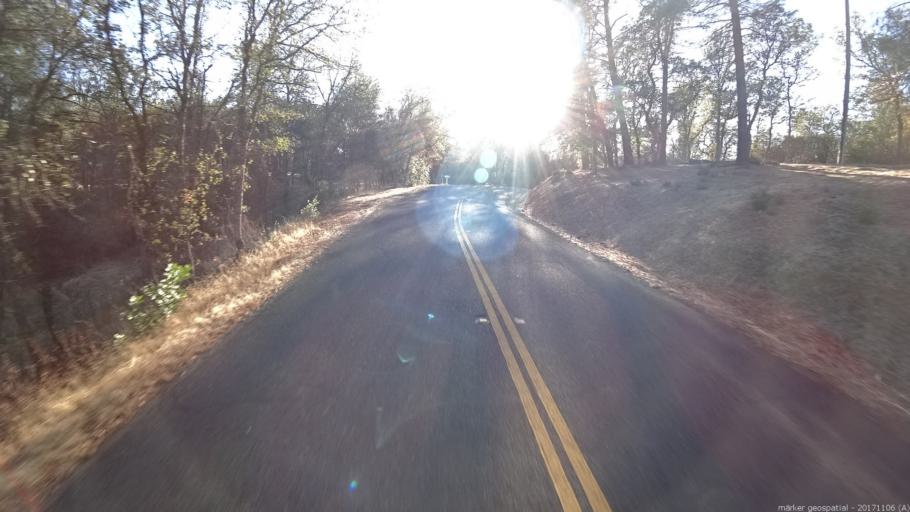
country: US
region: California
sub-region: Shasta County
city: Shasta
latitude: 40.5791
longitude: -122.4525
